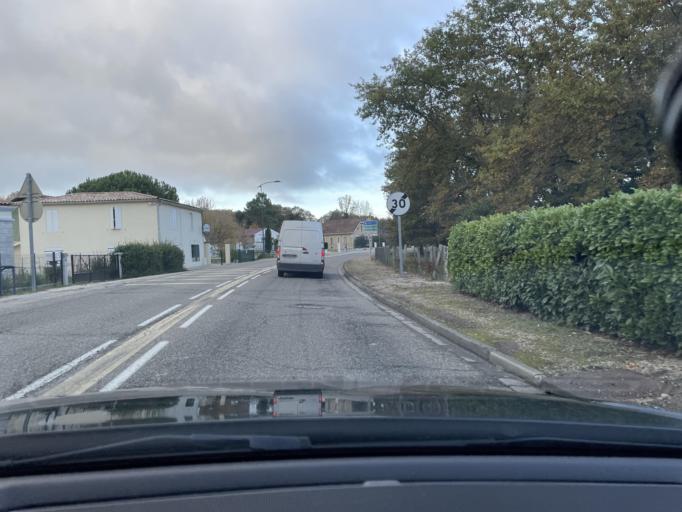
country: FR
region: Aquitaine
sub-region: Departement du Lot-et-Garonne
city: Casteljaloux
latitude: 44.3856
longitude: 0.1039
